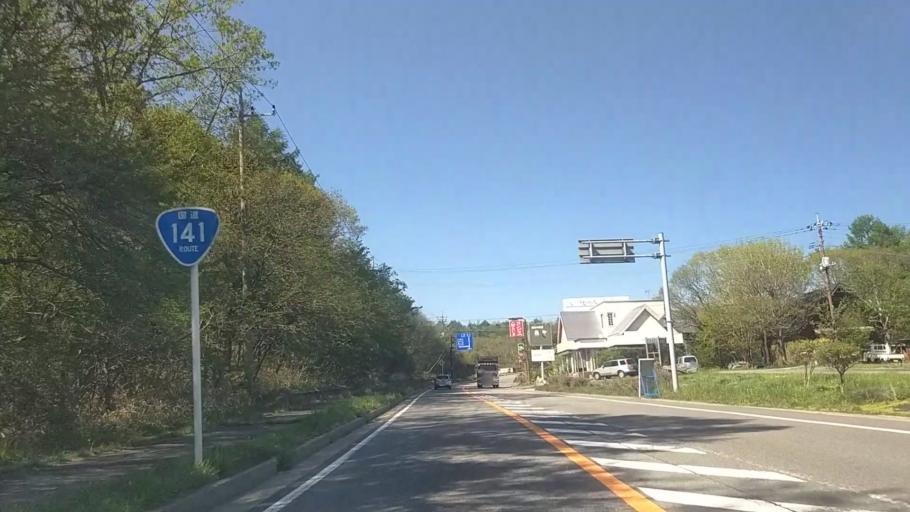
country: JP
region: Yamanashi
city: Nirasaki
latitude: 35.9286
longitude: 138.4427
